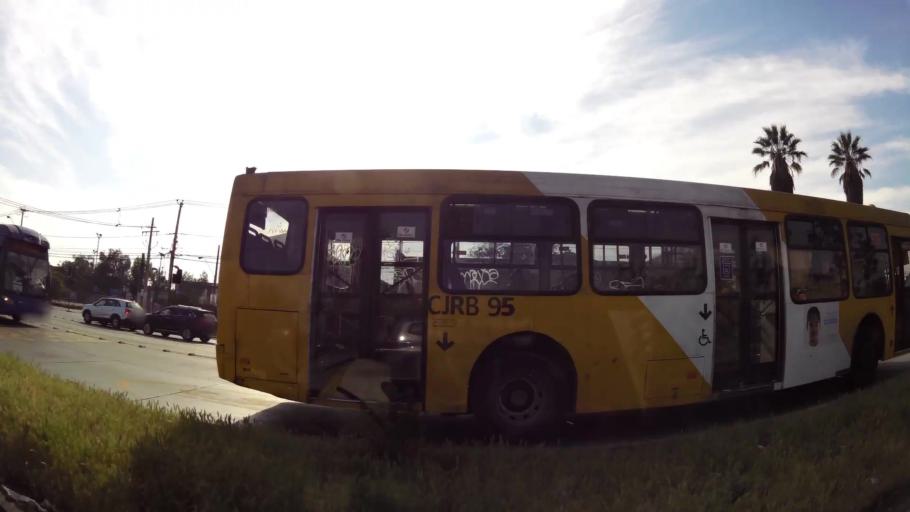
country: CL
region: Santiago Metropolitan
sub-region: Provincia de Santiago
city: La Pintana
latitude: -33.5518
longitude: -70.6325
